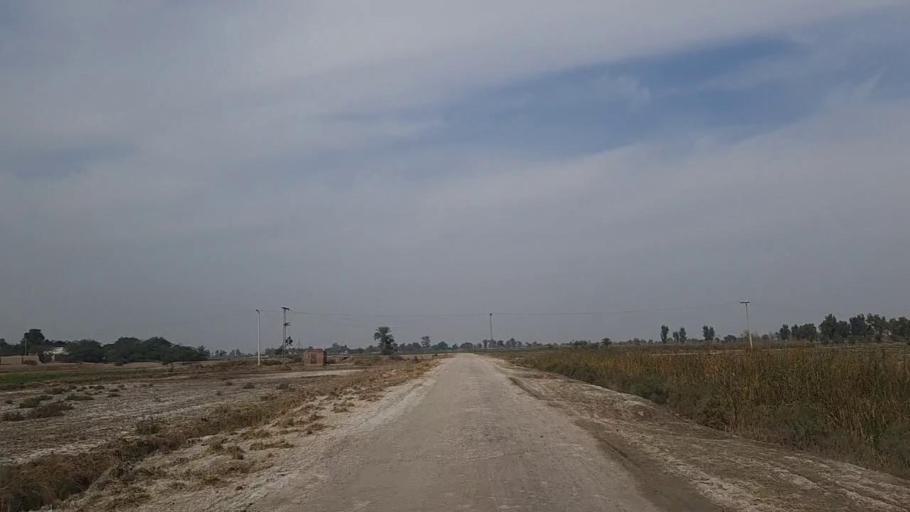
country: PK
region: Sindh
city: Daur
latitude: 26.4812
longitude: 68.4055
